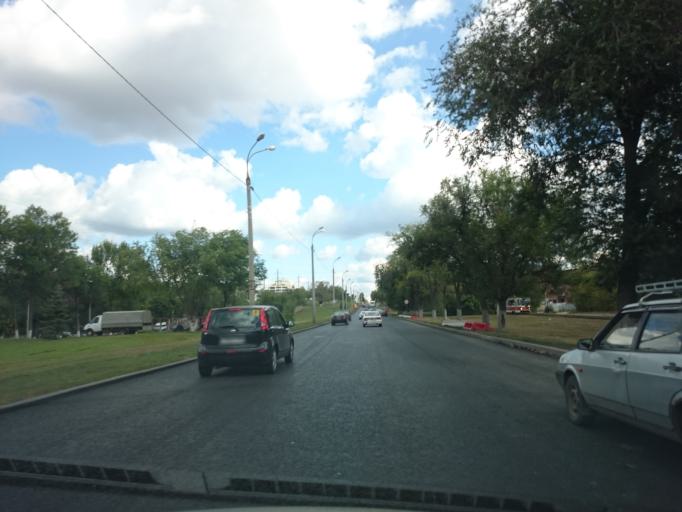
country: RU
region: Samara
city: Samara
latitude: 53.2249
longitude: 50.1718
